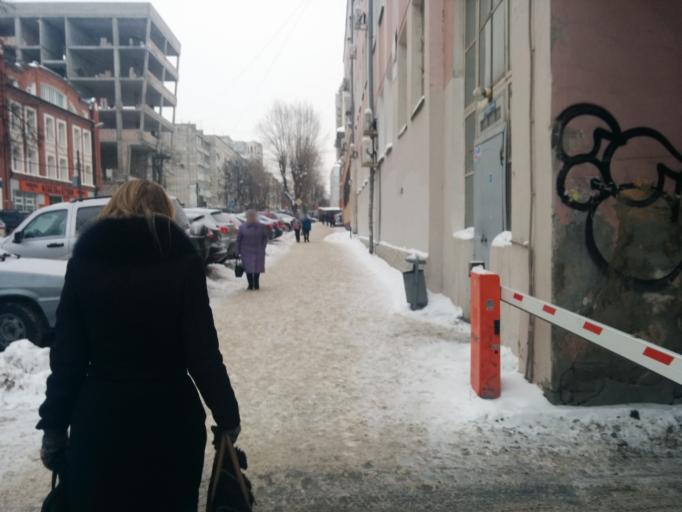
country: RU
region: Perm
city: Perm
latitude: 58.0140
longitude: 56.2493
